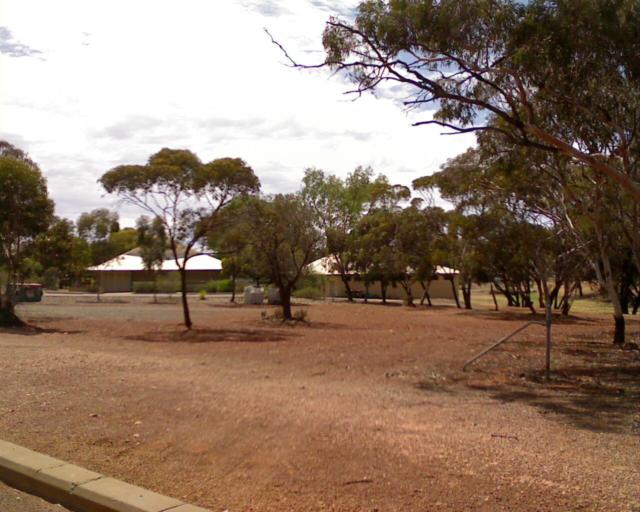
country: AU
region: Western Australia
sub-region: Kalgoorlie/Boulder
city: Stoneville
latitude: -31.2039
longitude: 121.6639
